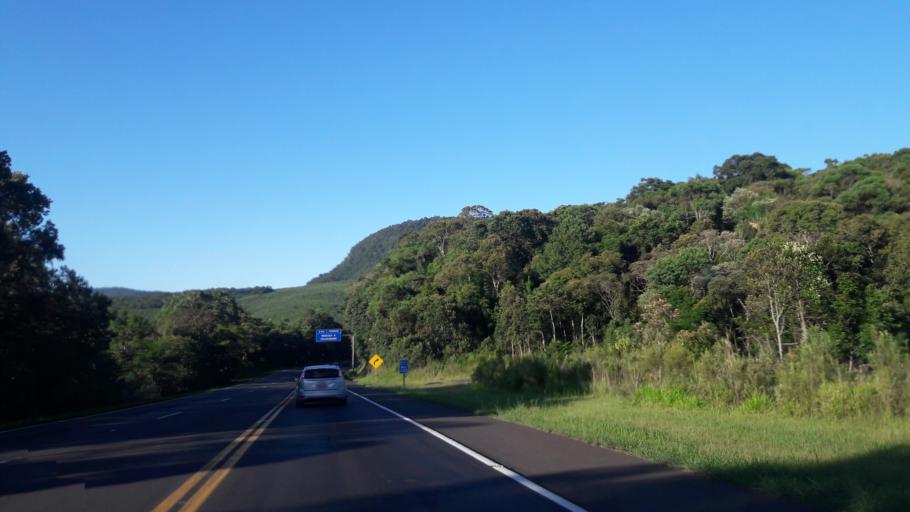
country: BR
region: Parana
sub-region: Prudentopolis
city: Prudentopolis
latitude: -25.3163
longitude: -51.1887
